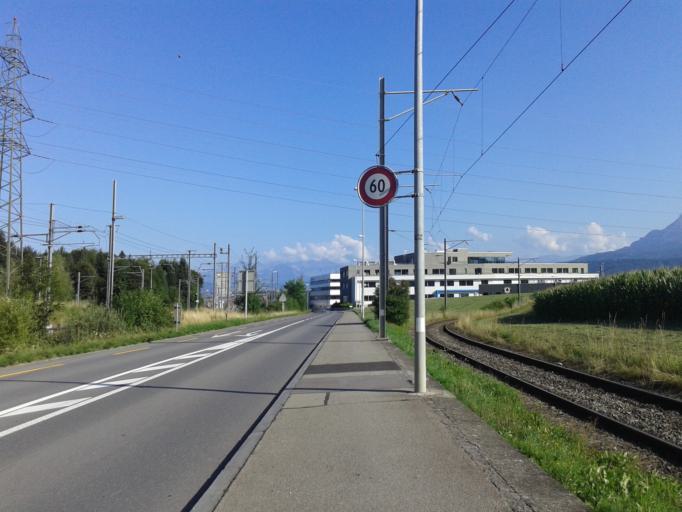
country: CH
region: Lucerne
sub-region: Sursee District
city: Neuenkirch
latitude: 47.0931
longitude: 8.2416
